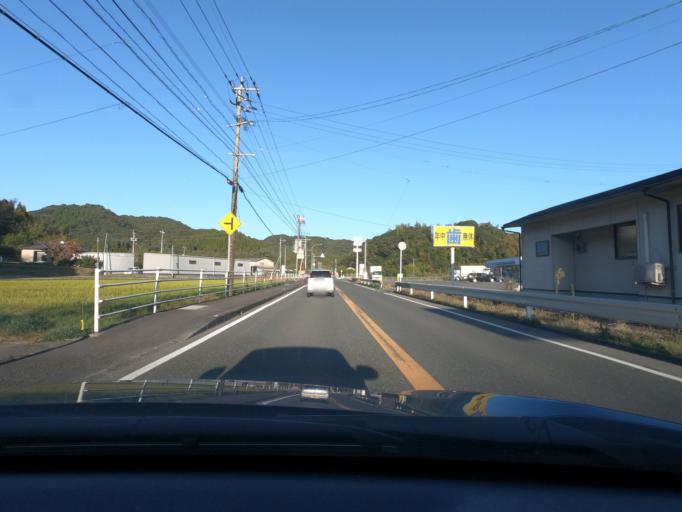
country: JP
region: Kagoshima
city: Satsumasendai
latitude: 31.8488
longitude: 130.2601
